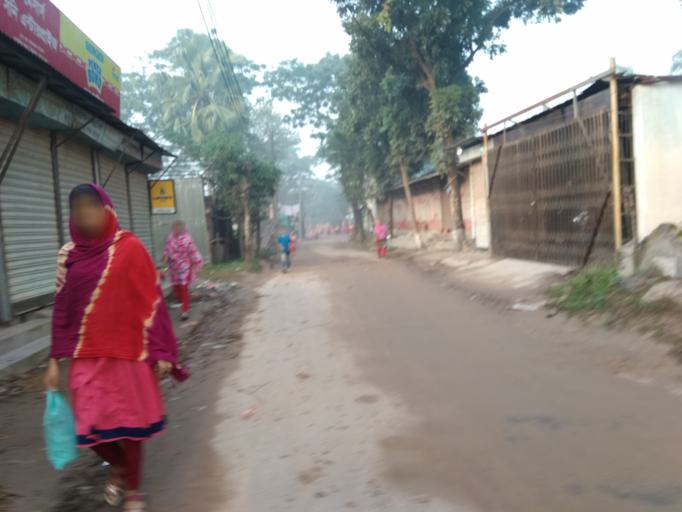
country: BD
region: Dhaka
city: Tungi
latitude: 23.8625
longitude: 90.4376
